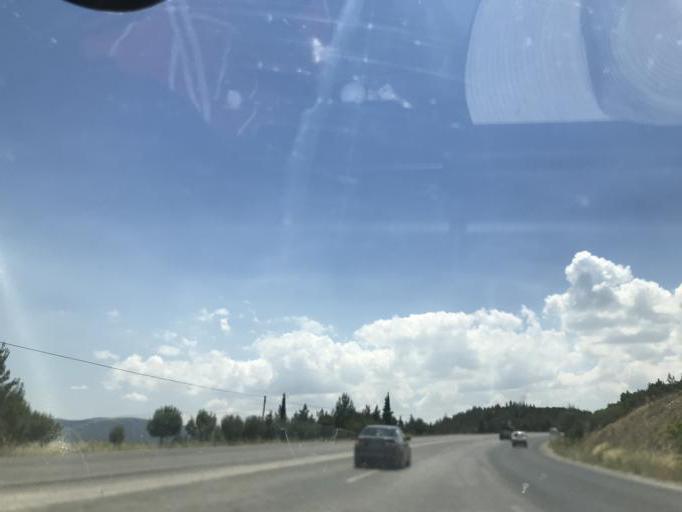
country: TR
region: Denizli
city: Honaz
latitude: 37.7070
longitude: 29.2048
